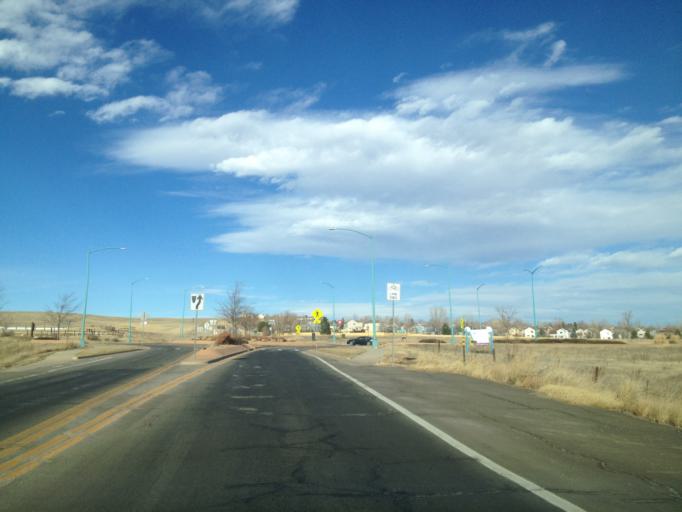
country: US
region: Colorado
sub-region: Boulder County
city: Superior
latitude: 39.9280
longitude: -105.1658
